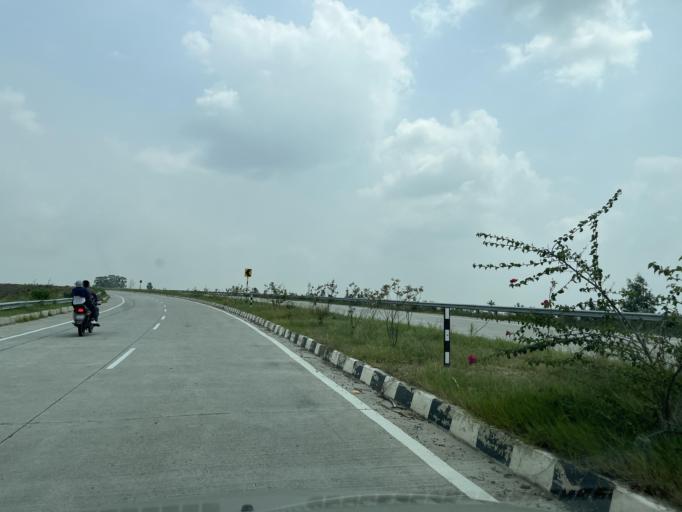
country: IN
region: Uttar Pradesh
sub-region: Bijnor
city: Nagina
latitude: 29.4250
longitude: 78.4246
